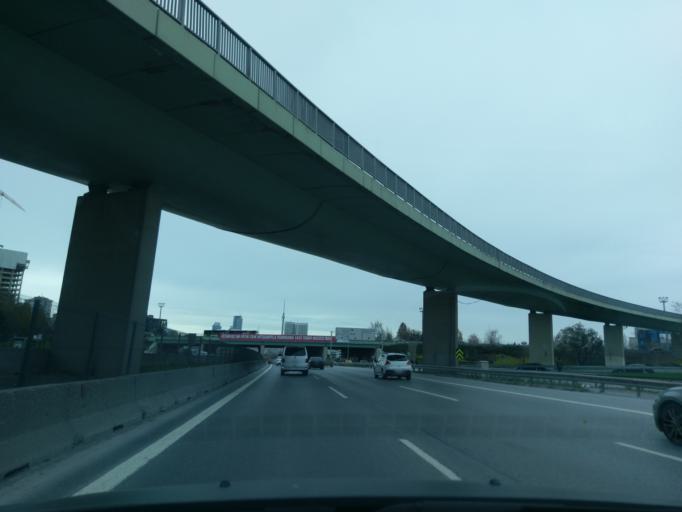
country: TR
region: Istanbul
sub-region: Atasehir
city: Atasehir
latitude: 40.9800
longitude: 29.0961
